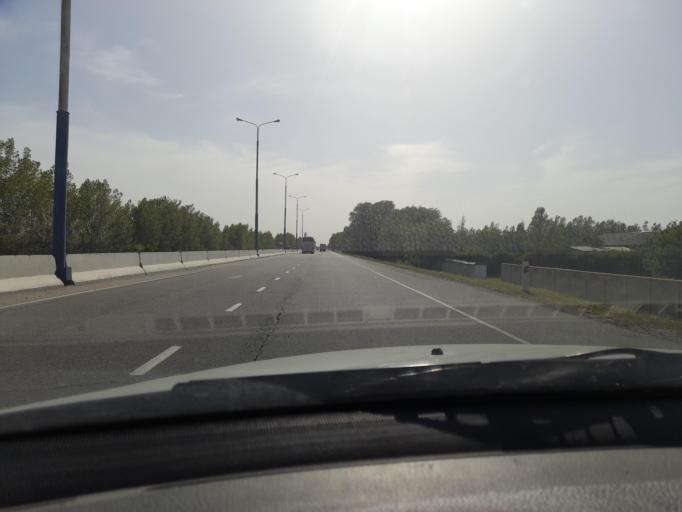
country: UZ
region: Samarqand
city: Ishtixon
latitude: 39.9475
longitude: 66.4173
